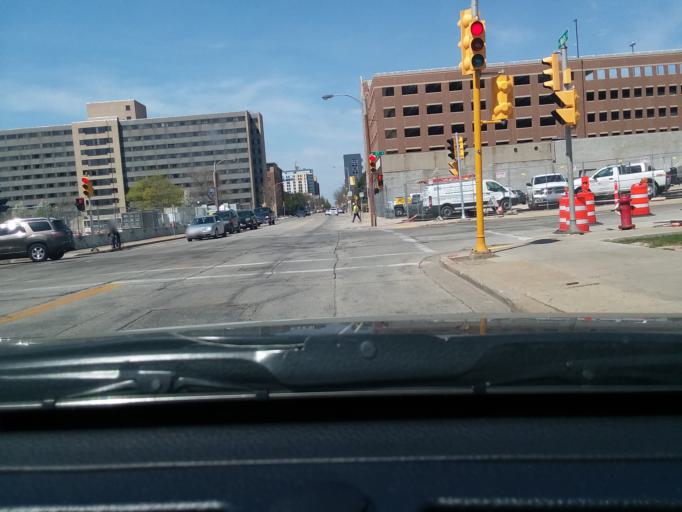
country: US
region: Wisconsin
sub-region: Milwaukee County
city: Milwaukee
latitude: 43.0403
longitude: -87.9269
